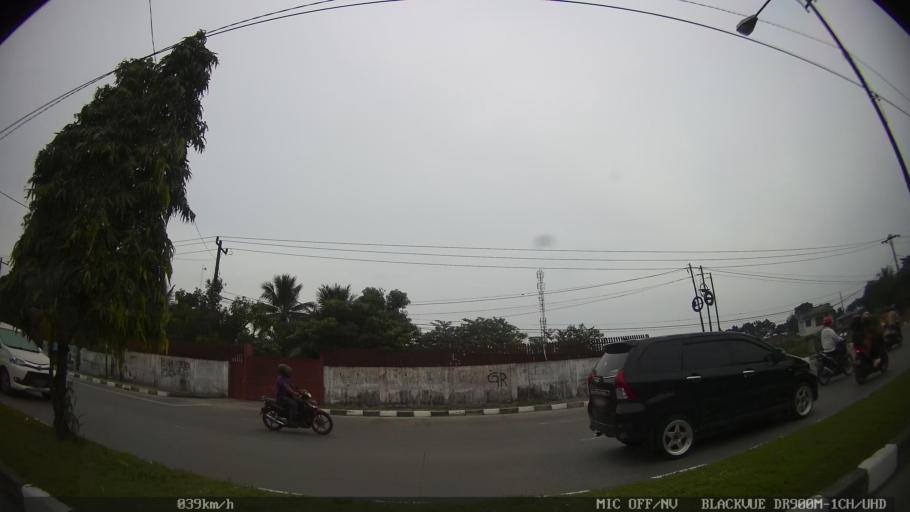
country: ID
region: North Sumatra
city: Deli Tua
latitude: 3.5406
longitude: 98.6995
